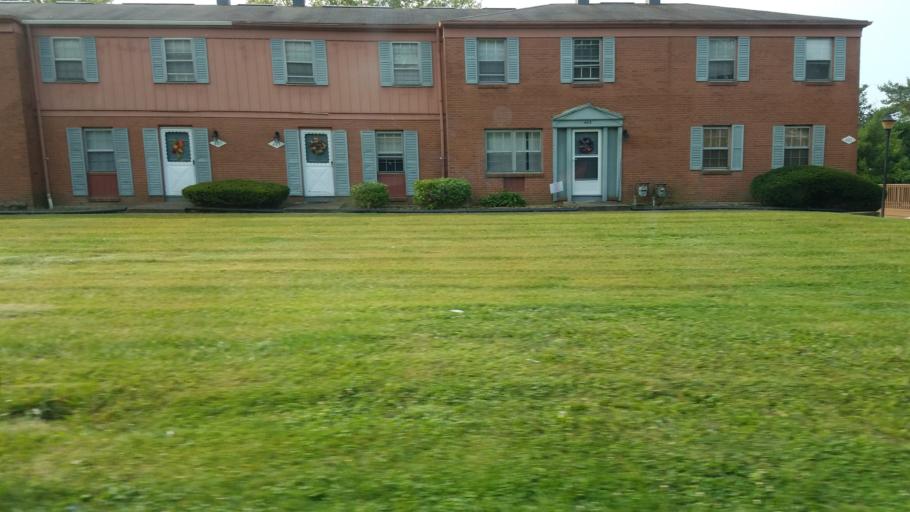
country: US
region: Ohio
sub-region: Mahoning County
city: Boardman
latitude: 41.0389
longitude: -80.6456
